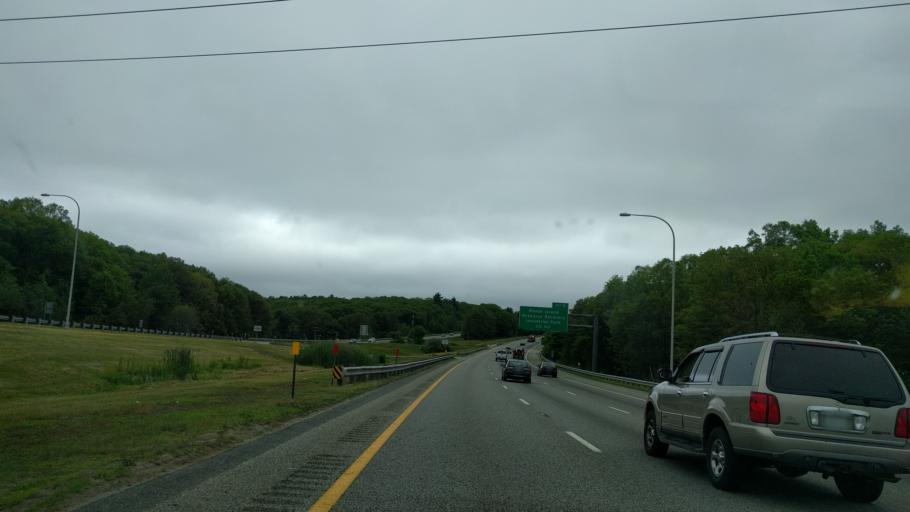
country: US
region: Rhode Island
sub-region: Providence County
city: Johnston
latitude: 41.8138
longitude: -71.5098
